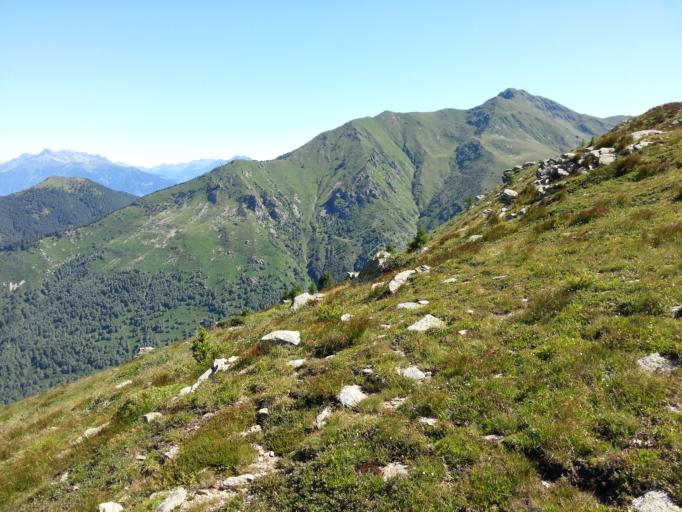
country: CH
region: Ticino
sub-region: Bellinzona District
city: Camorino
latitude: 46.1123
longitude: 9.0257
